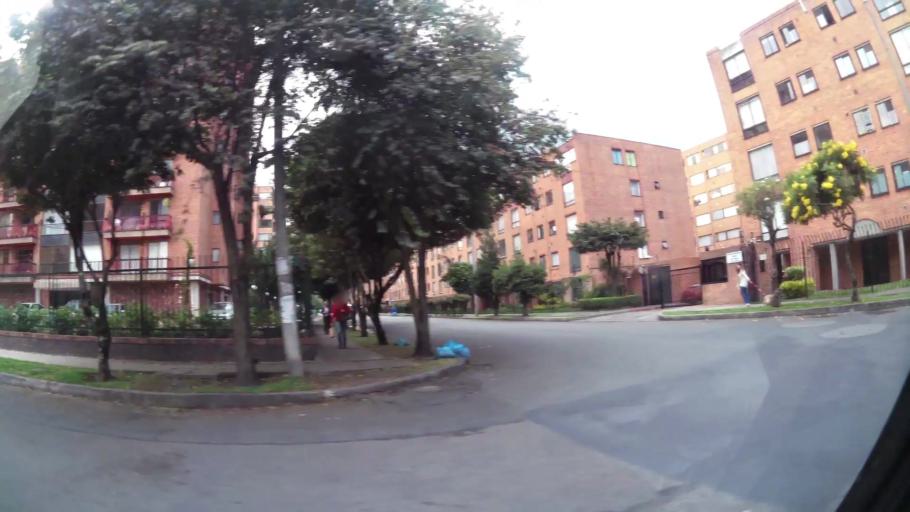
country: CO
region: Bogota D.C.
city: Barrio San Luis
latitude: 4.7271
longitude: -74.0687
